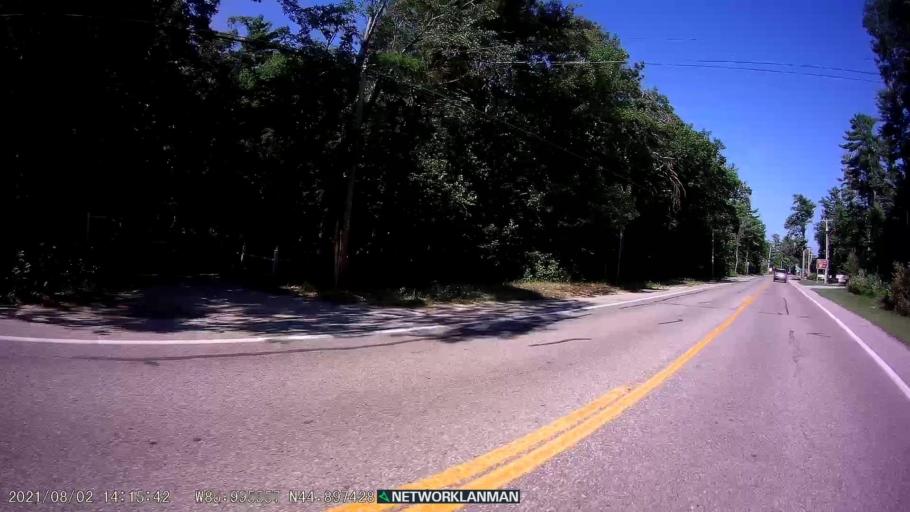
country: US
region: Michigan
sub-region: Leelanau County
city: Leland
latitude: 44.8975
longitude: -85.9953
